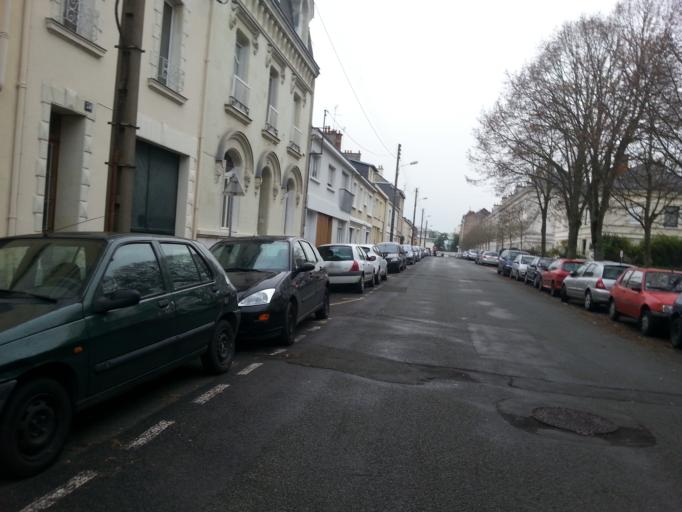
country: FR
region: Pays de la Loire
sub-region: Departement de Maine-et-Loire
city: Angers
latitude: 47.4624
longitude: -0.5584
